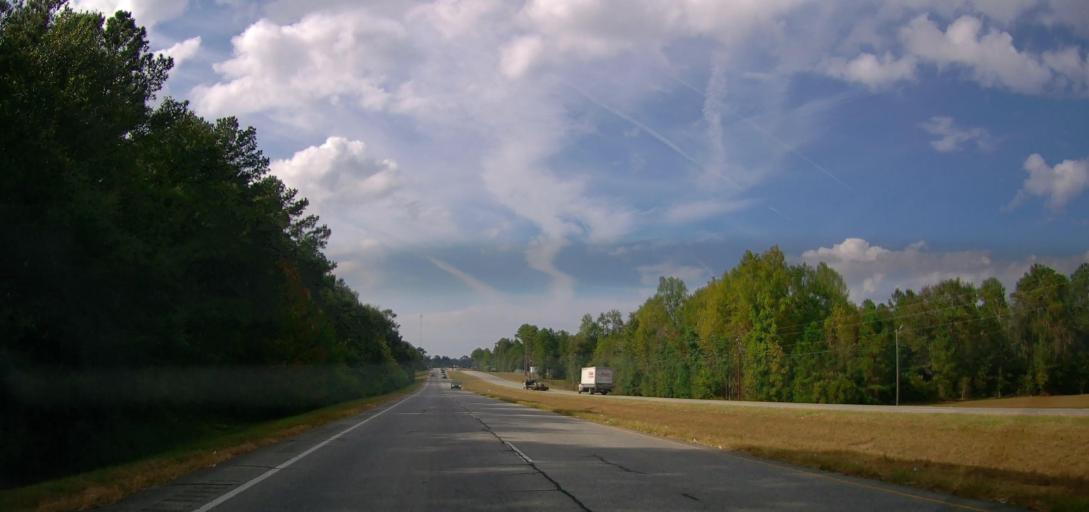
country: US
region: Georgia
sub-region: Mitchell County
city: Pelham
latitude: 31.1141
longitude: -84.1290
